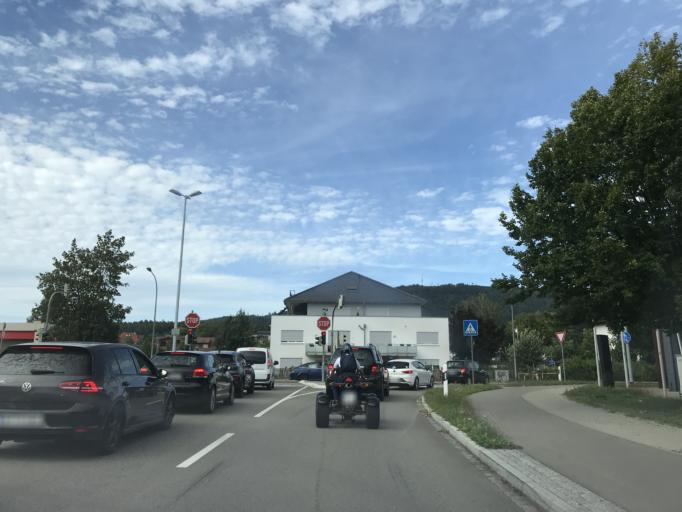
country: DE
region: Baden-Wuerttemberg
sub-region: Freiburg Region
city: Bad Sackingen
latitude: 47.5533
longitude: 7.9365
